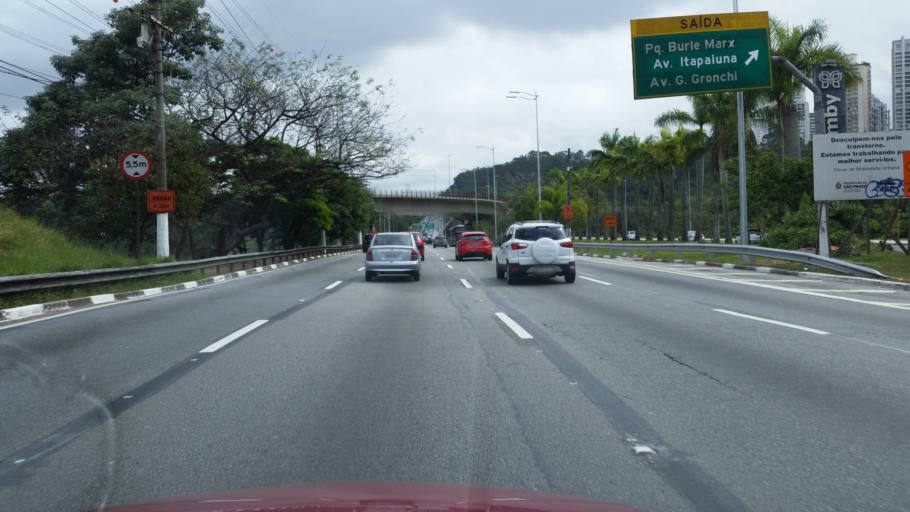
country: BR
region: Sao Paulo
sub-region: Taboao Da Serra
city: Taboao da Serra
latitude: -23.6320
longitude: -46.7185
